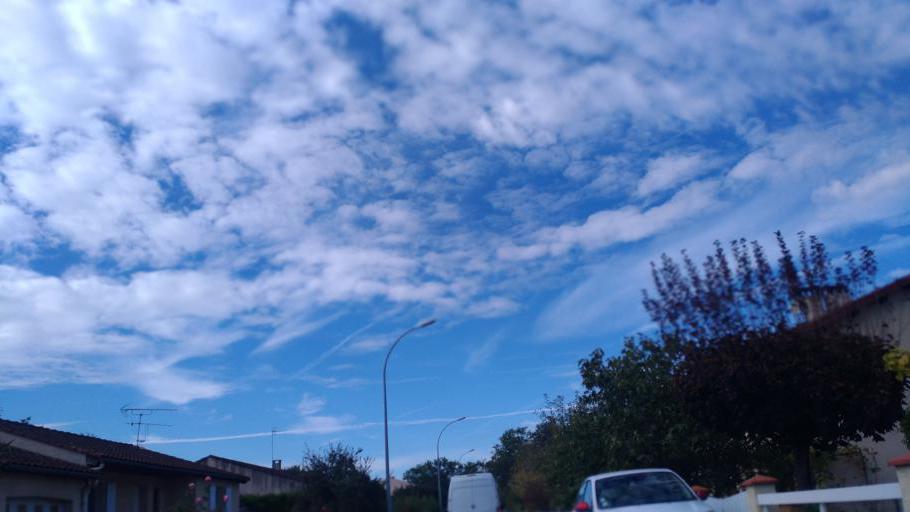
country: FR
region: Midi-Pyrenees
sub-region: Departement du Tarn
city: Puygouzon
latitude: 43.9149
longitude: 2.1707
